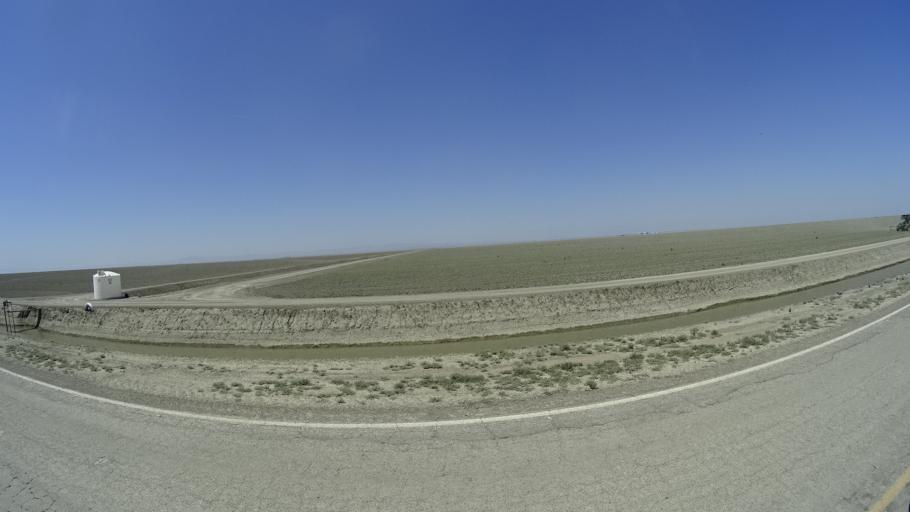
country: US
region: California
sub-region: Kings County
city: Corcoran
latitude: 36.0001
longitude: -119.6432
